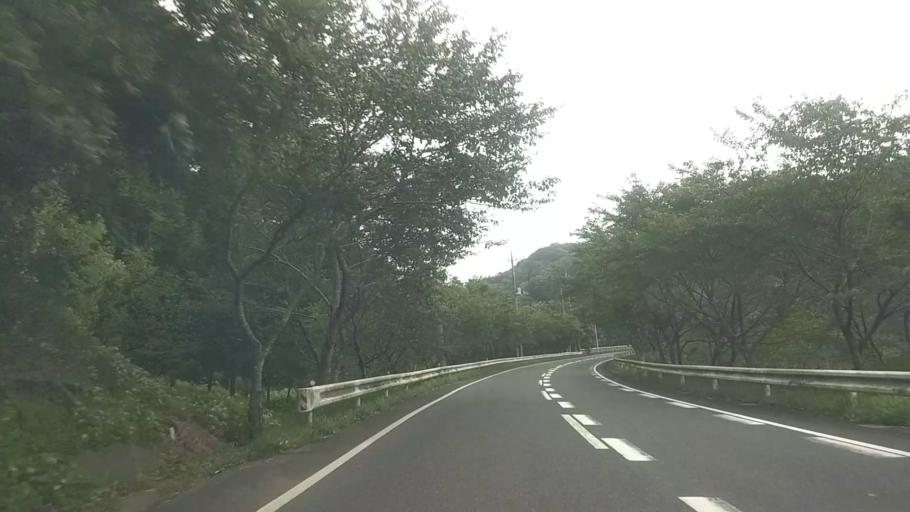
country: JP
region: Chiba
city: Kimitsu
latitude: 35.2353
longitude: 139.9698
